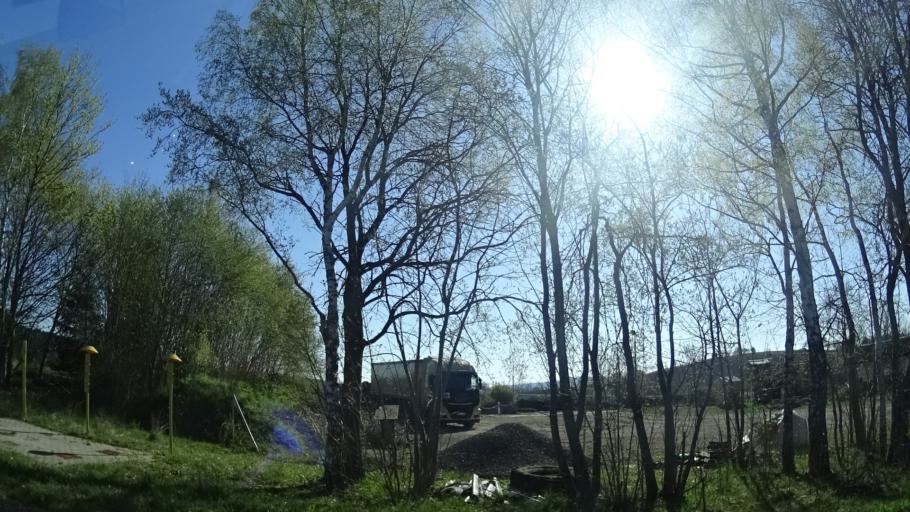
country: DE
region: Thuringia
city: Bohlen
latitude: 50.5918
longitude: 11.0427
